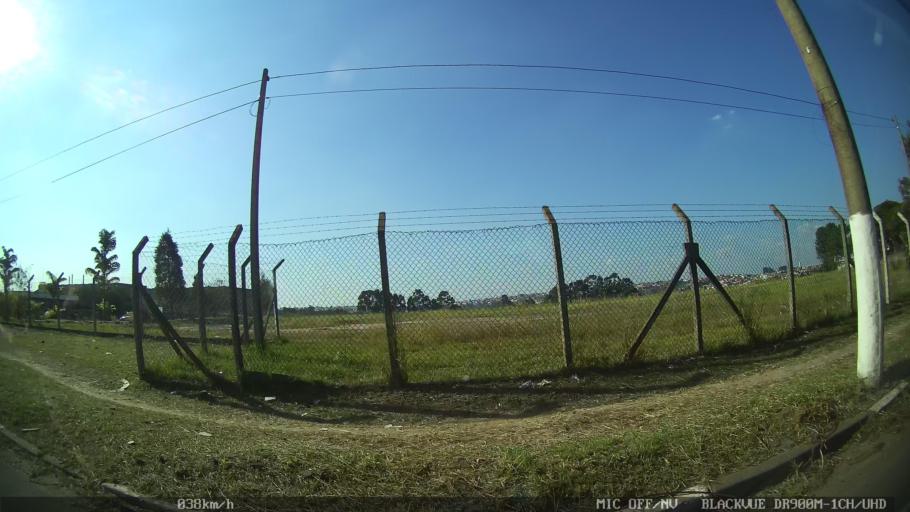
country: BR
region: Sao Paulo
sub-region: Campinas
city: Campinas
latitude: -22.9936
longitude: -47.1328
